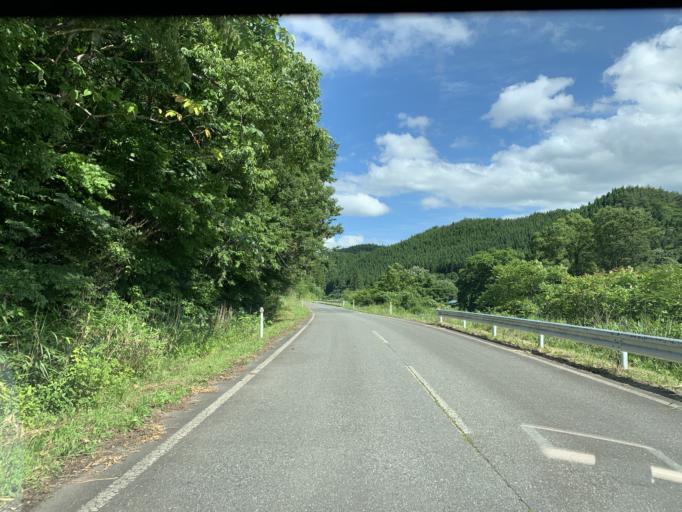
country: JP
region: Iwate
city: Ichinoseki
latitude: 38.9630
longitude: 140.9657
